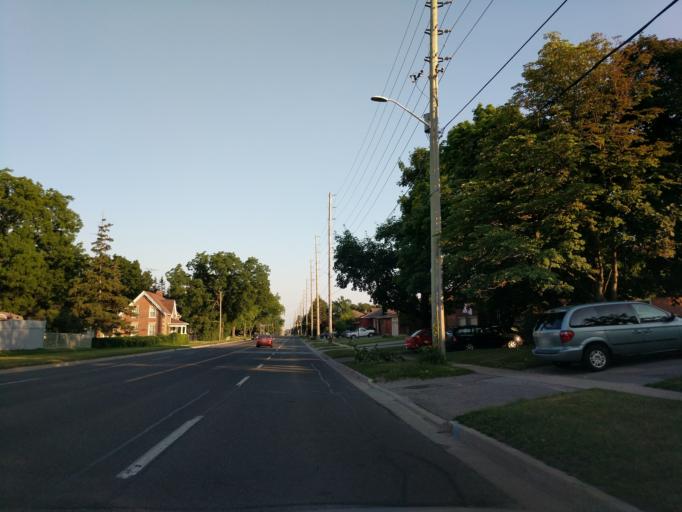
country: CA
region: Ontario
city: Oshawa
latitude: 43.8995
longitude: -78.8970
